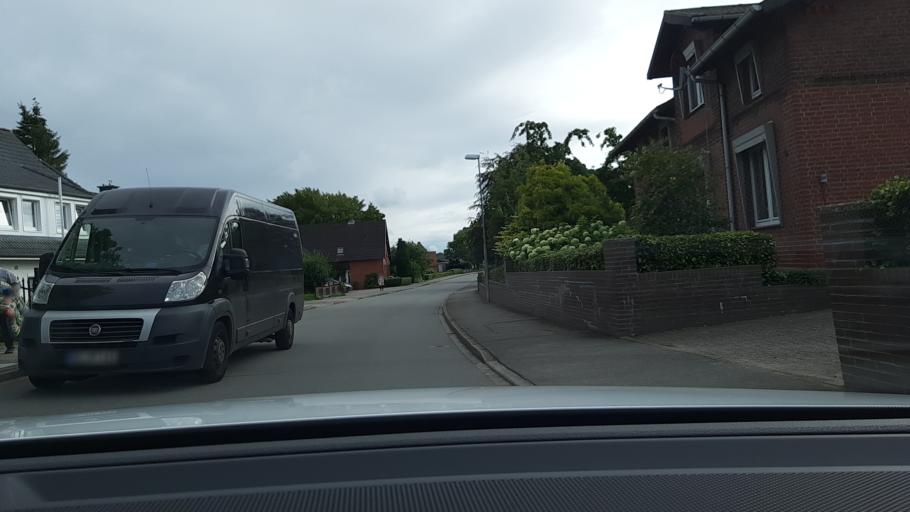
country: DE
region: Schleswig-Holstein
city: Badendorf
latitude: 53.8687
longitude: 10.5814
